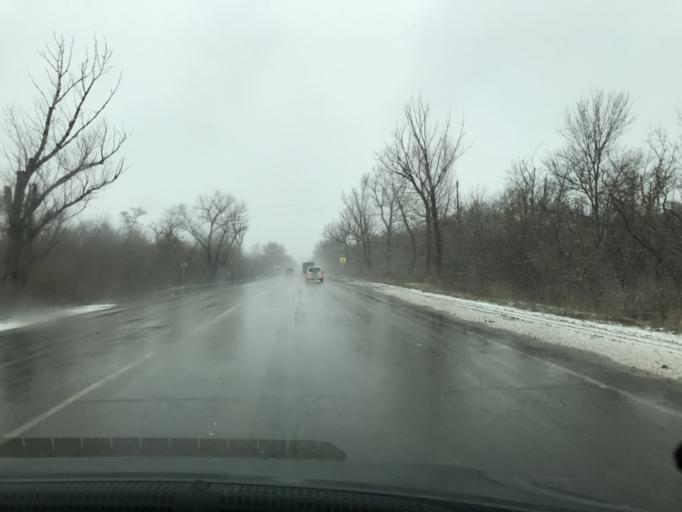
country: RU
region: Rostov
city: Bataysk
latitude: 47.0503
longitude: 39.8381
